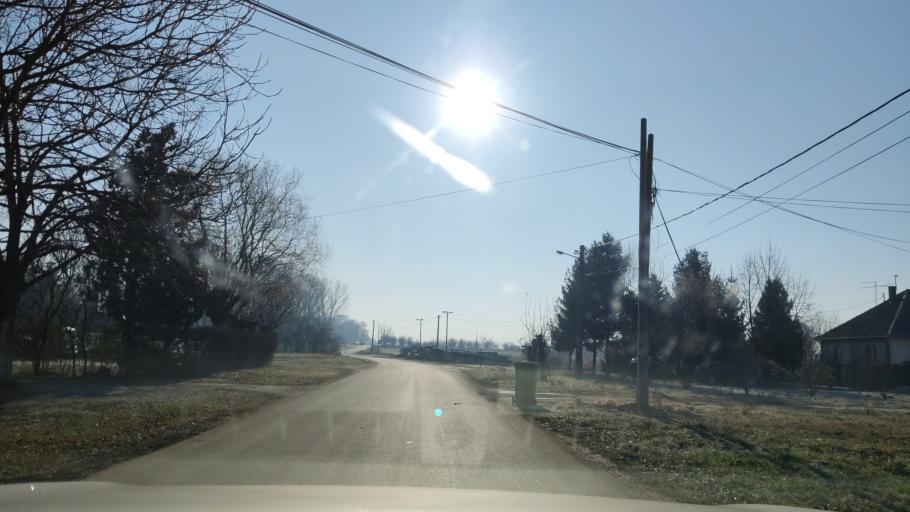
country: RS
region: Central Serbia
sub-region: Belgrade
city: Surcin
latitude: 44.7464
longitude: 20.2703
